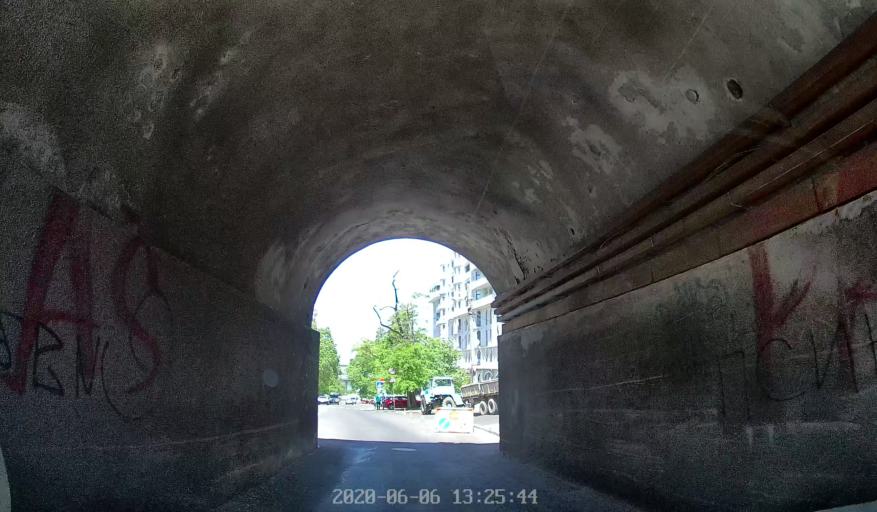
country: NG
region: Niger
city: Lemu
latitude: 9.2976
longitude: 6.1474
